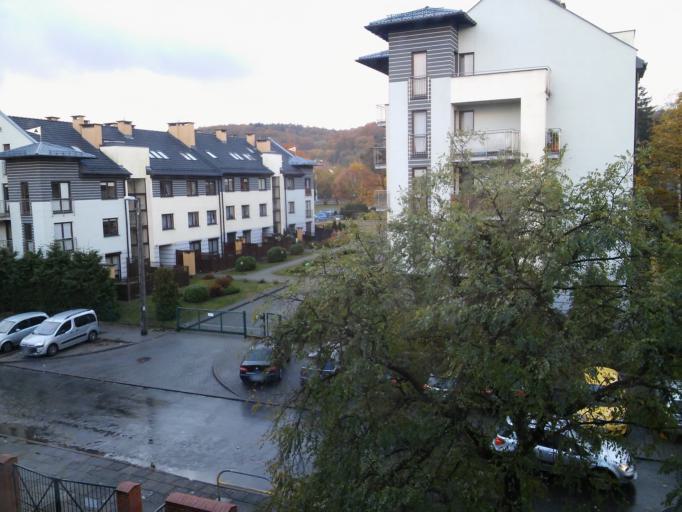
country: PL
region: Pomeranian Voivodeship
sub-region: Sopot
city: Sopot
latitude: 54.4041
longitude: 18.5672
